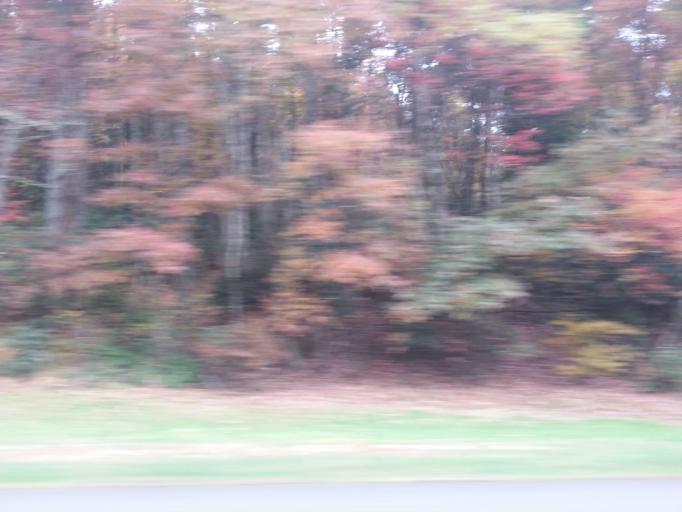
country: US
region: North Carolina
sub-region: Wilkes County
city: Millers Creek
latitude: 36.2845
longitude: -81.3734
